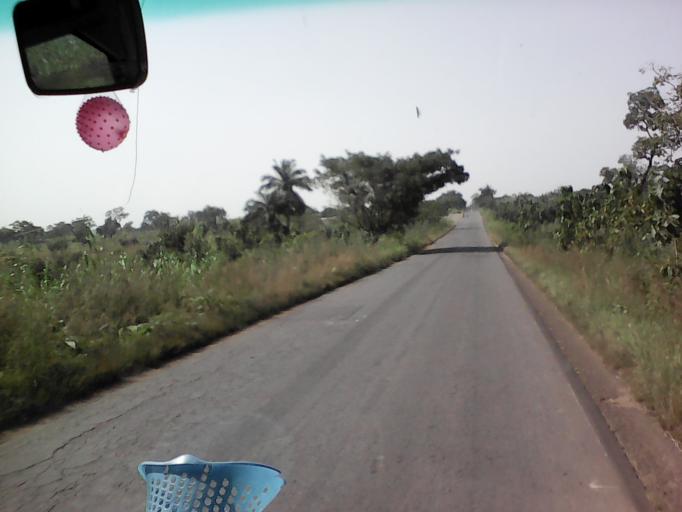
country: TG
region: Centrale
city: Sokode
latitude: 8.8543
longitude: 1.0747
